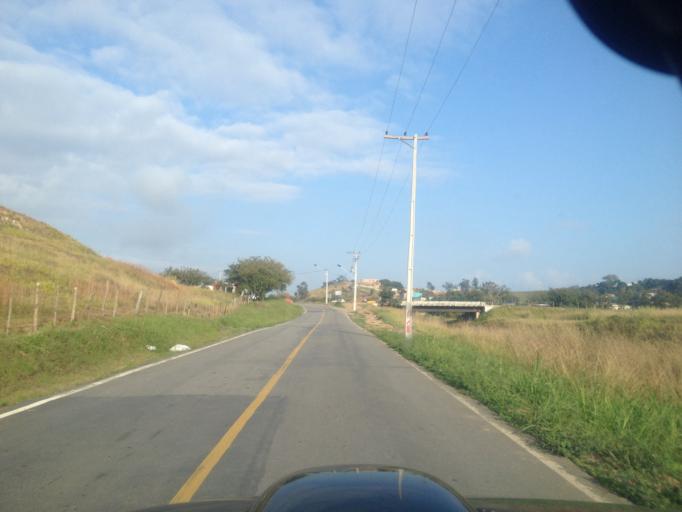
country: BR
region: Rio de Janeiro
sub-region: Porto Real
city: Porto Real
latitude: -22.4452
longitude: -44.3148
